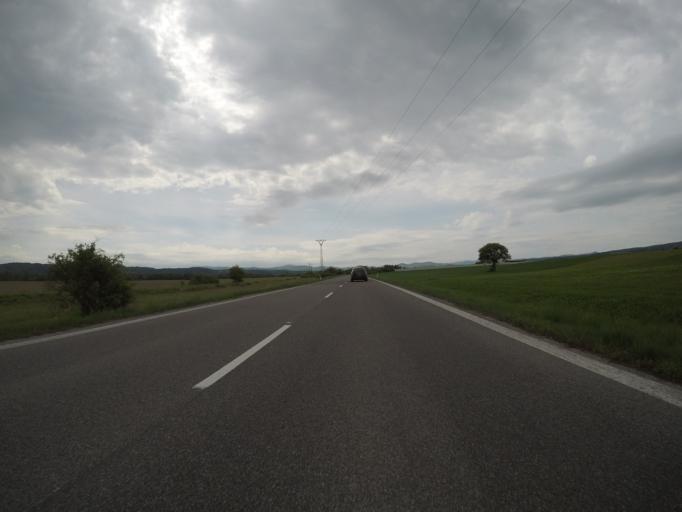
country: SK
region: Banskobystricky
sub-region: Okres Banska Bystrica
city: Zvolen
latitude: 48.6488
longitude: 19.1423
